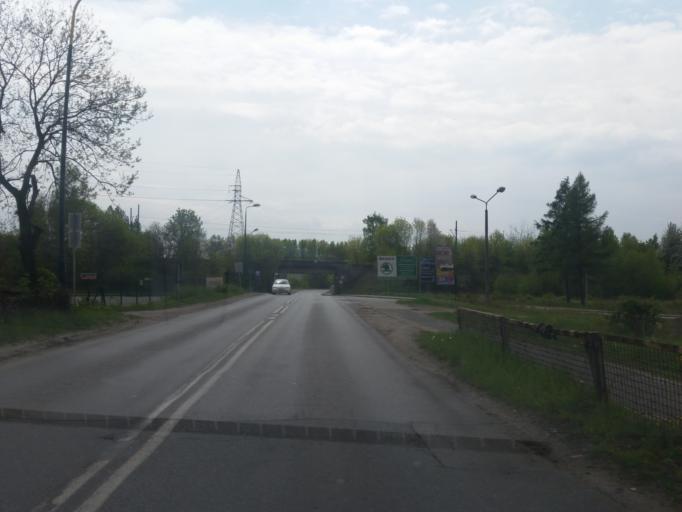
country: PL
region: Silesian Voivodeship
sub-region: Sosnowiec
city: Sosnowiec
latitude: 50.2642
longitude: 19.1384
